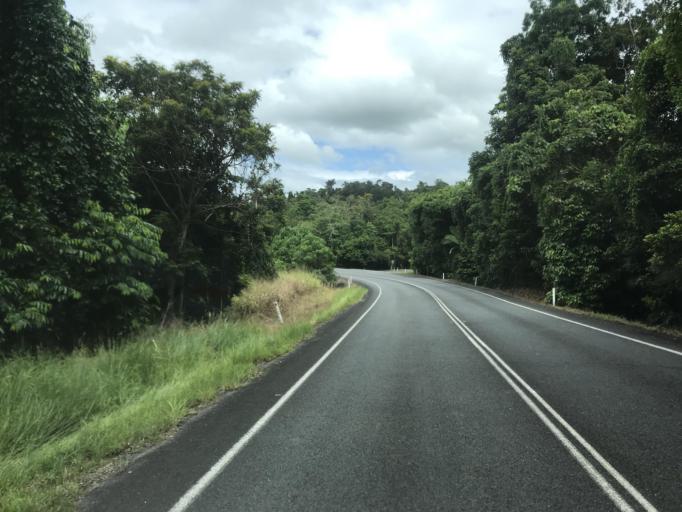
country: AU
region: Queensland
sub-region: Cassowary Coast
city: Innisfail
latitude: -17.8522
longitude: 146.0657
